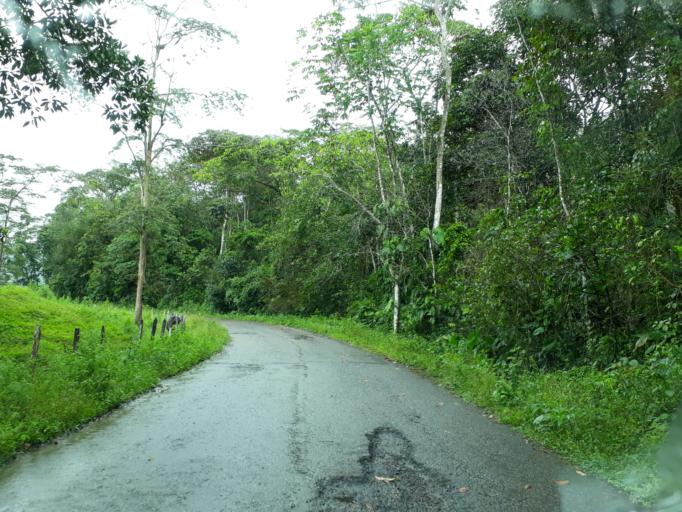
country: CO
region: Boyaca
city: Santa Maria
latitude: 4.6938
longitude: -73.3054
